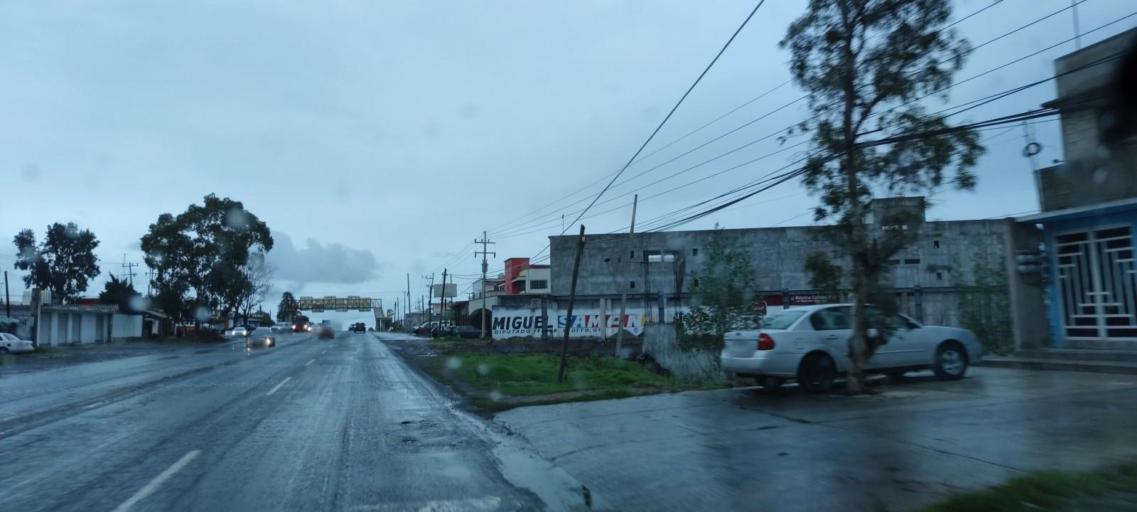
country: MX
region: Mexico
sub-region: Jilotepec
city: Doxhicho
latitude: 19.9472
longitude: -99.5545
